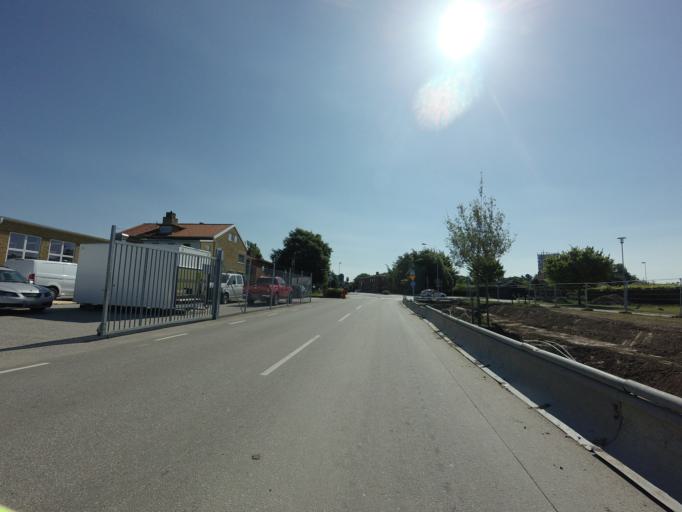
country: SE
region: Skane
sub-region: Vellinge Kommun
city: Vellinge
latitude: 55.4720
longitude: 13.0136
